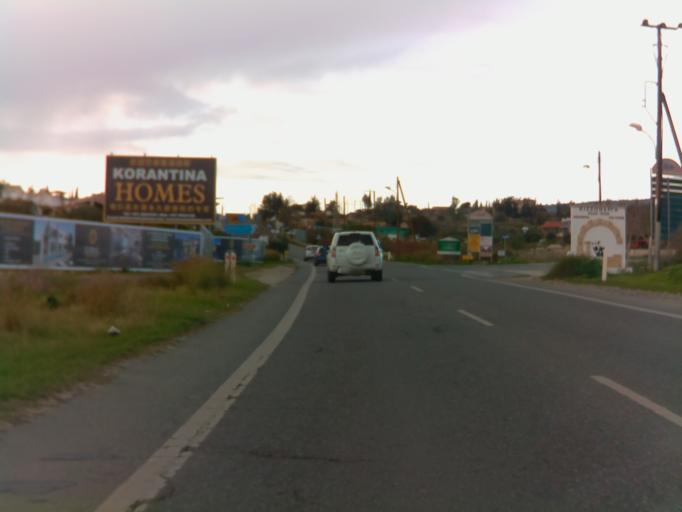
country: CY
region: Pafos
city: Kissonerga
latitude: 34.8501
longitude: 32.3842
